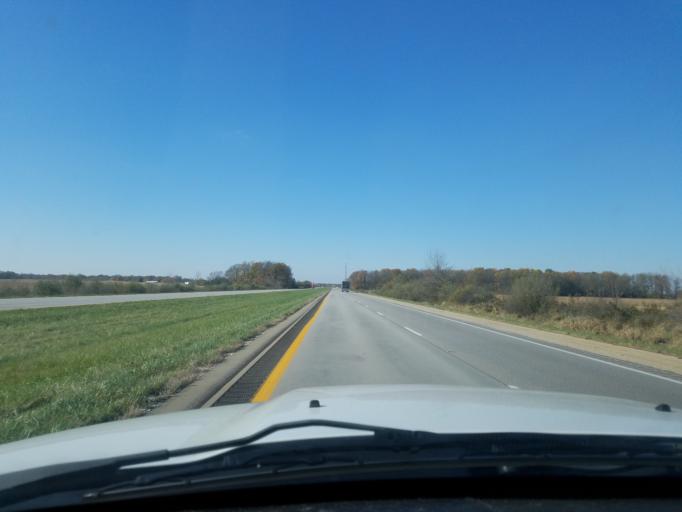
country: US
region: Indiana
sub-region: Montgomery County
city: Crawfordsville
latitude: 40.0123
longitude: -86.7610
